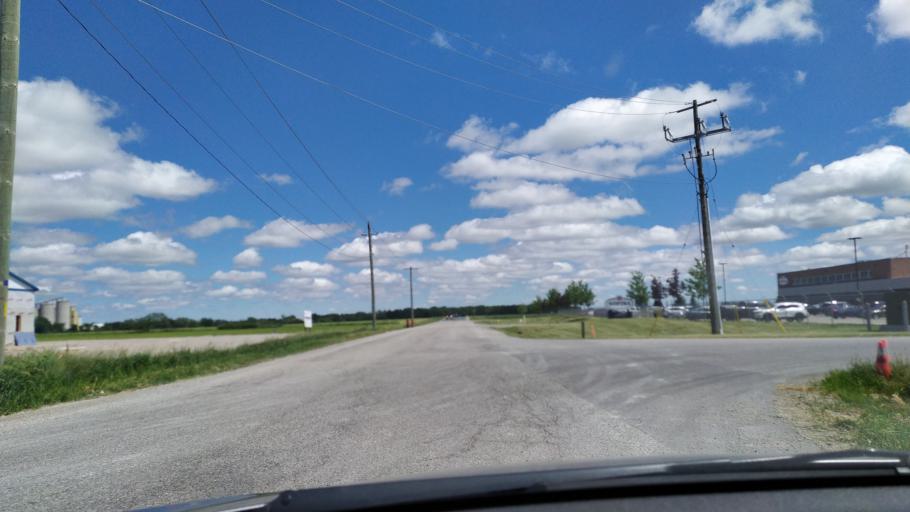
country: CA
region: Ontario
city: Huron East
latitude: 43.4556
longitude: -81.1938
